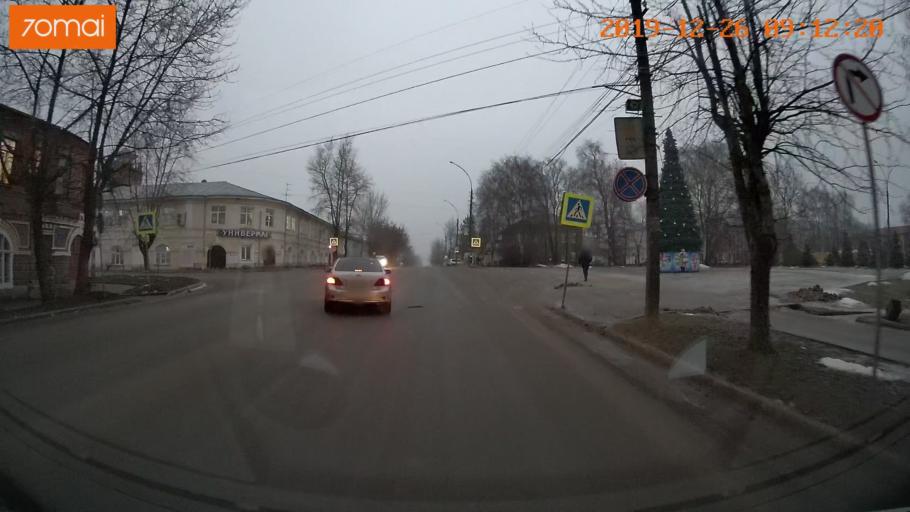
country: RU
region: Vologda
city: Gryazovets
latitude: 58.8804
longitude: 40.2533
